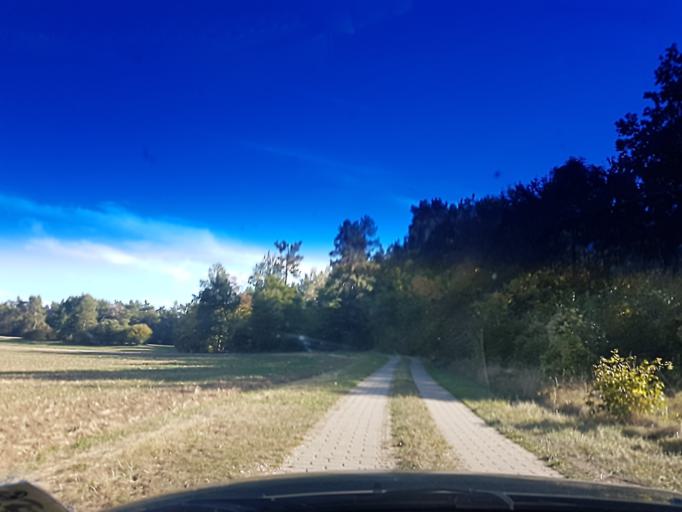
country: DE
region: Bavaria
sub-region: Upper Franconia
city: Schesslitz
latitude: 49.9875
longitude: 11.0860
